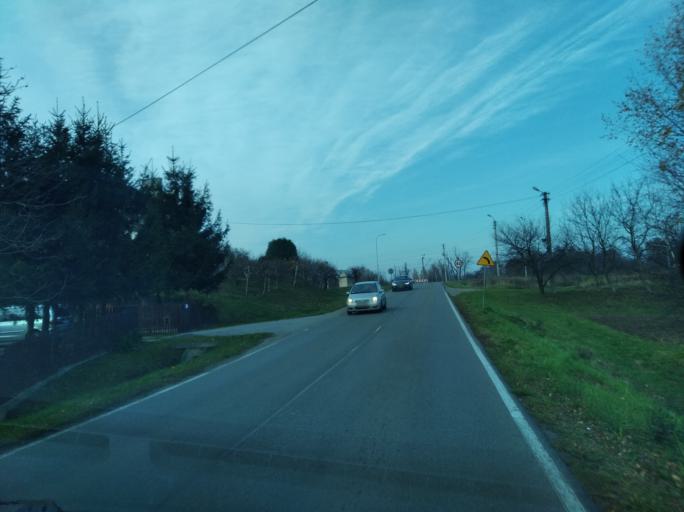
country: PL
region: Subcarpathian Voivodeship
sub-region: Powiat ropczycko-sedziszowski
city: Sedziszow Malopolski
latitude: 50.0688
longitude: 21.7290
